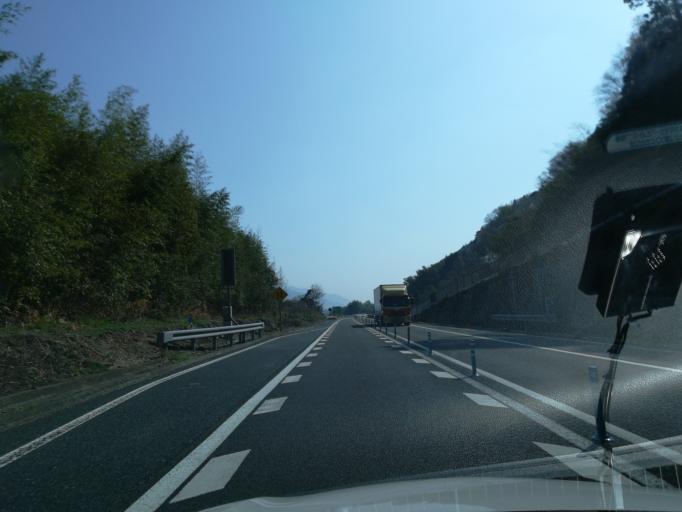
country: JP
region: Tokushima
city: Ikedacho
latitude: 34.0308
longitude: 133.8504
